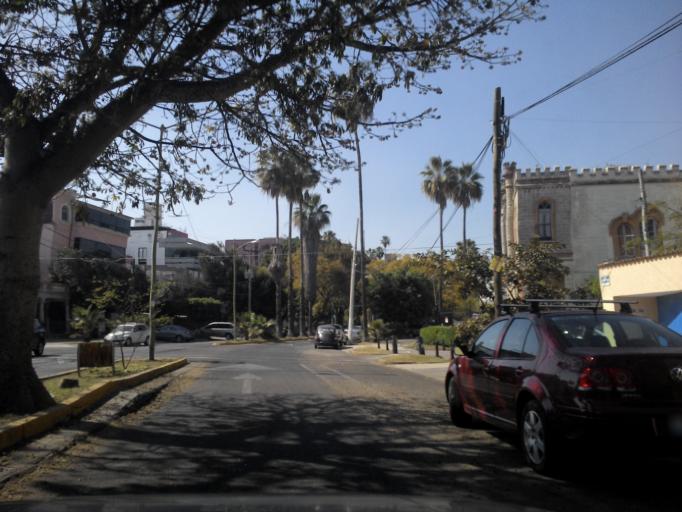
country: MX
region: Jalisco
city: Guadalajara
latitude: 20.6717
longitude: -103.3614
